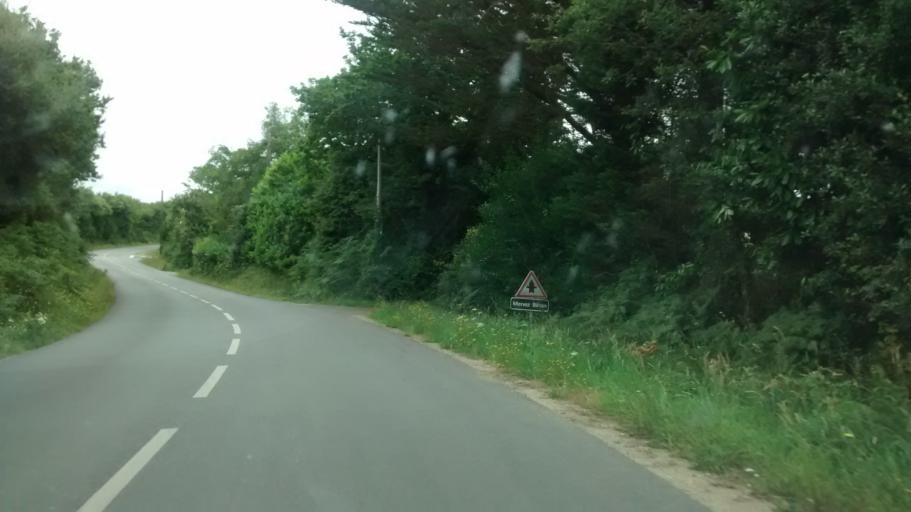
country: FR
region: Brittany
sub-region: Departement du Finistere
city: Plougastel-Daoulas
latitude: 48.3400
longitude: -4.4215
